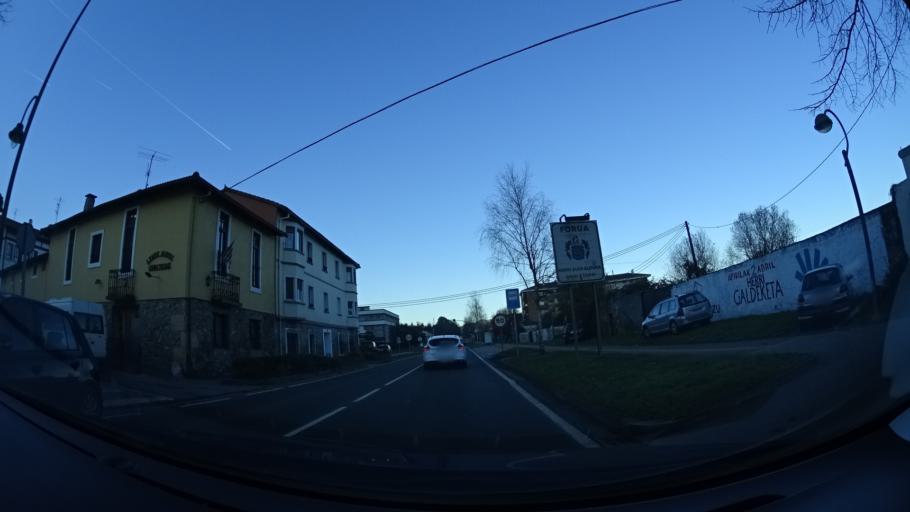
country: ES
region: Basque Country
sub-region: Bizkaia
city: Gernika-Lumo
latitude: 43.3238
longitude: -2.6780
